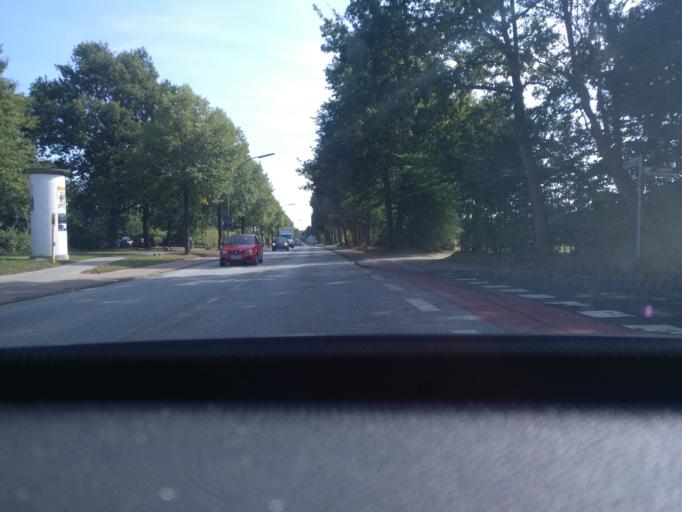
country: DE
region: Schleswig-Holstein
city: Norderstedt
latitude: 53.6716
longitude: 9.9691
